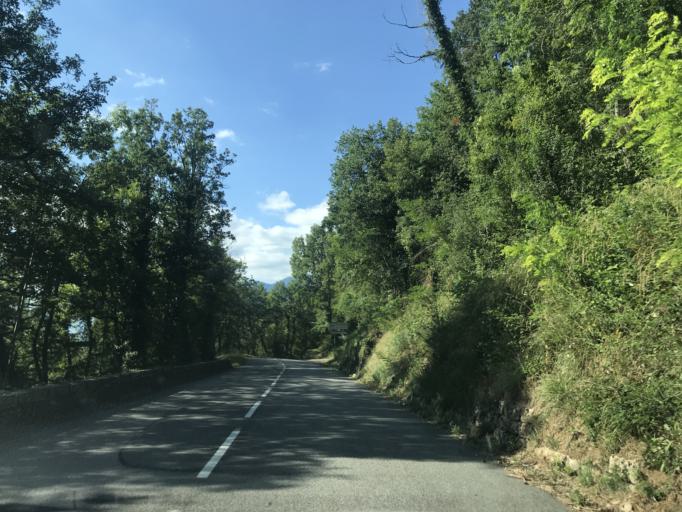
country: FR
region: Rhone-Alpes
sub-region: Departement de l'Ain
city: Culoz
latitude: 45.7988
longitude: 5.7869
